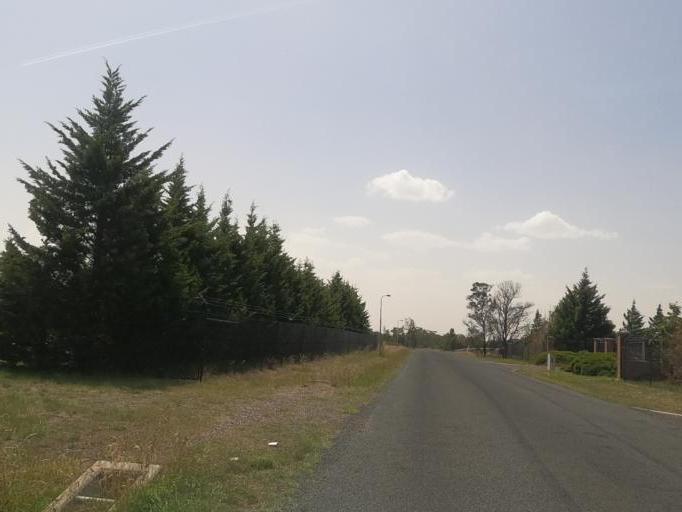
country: AU
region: Victoria
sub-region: Hume
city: Craigieburn
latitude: -37.5637
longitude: 144.8967
